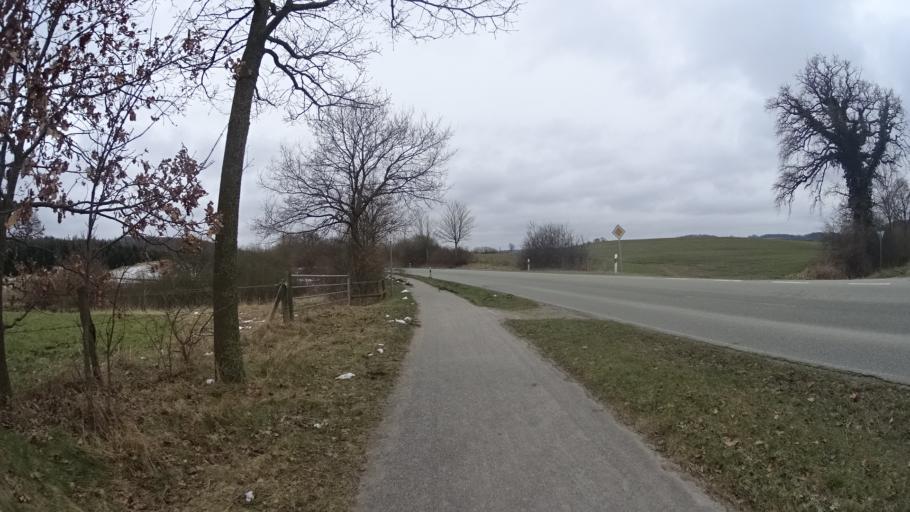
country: DE
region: Schleswig-Holstein
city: Neukirchen
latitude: 54.1976
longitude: 10.5612
